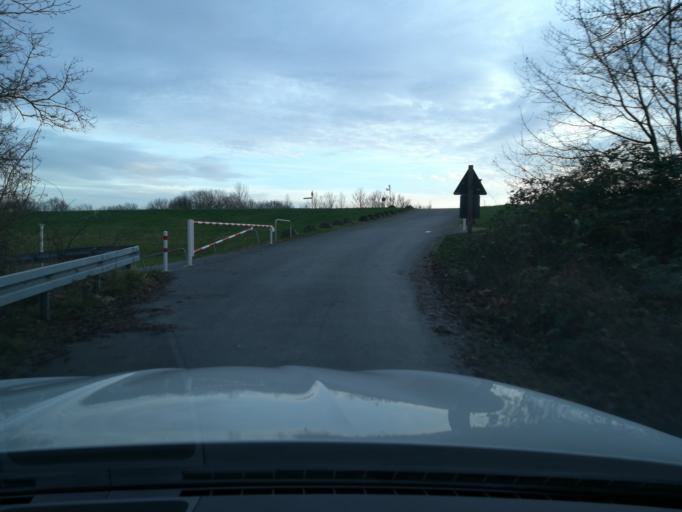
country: DE
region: Hamburg
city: Harburg
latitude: 53.4693
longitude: 10.0056
